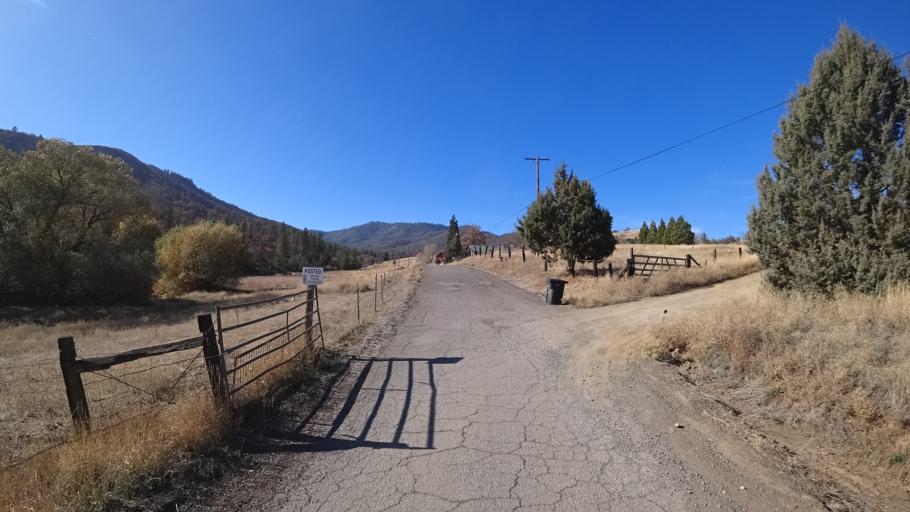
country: US
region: California
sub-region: Siskiyou County
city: Yreka
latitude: 41.7611
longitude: -122.6360
